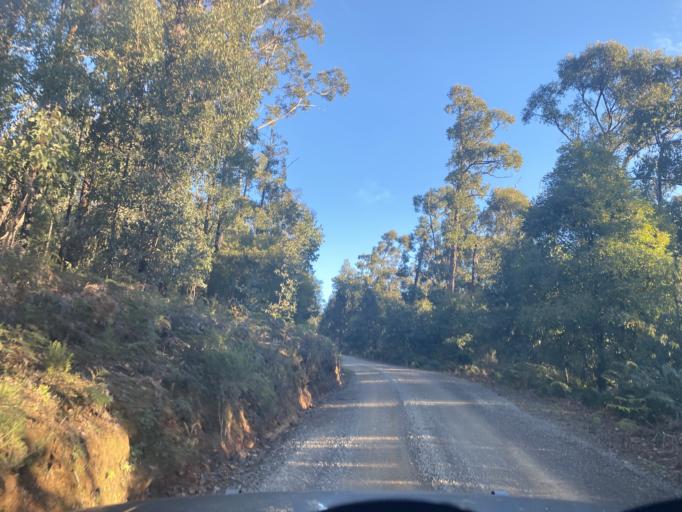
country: AU
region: Victoria
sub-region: Yarra Ranges
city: Healesville
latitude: -37.4196
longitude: 145.5300
